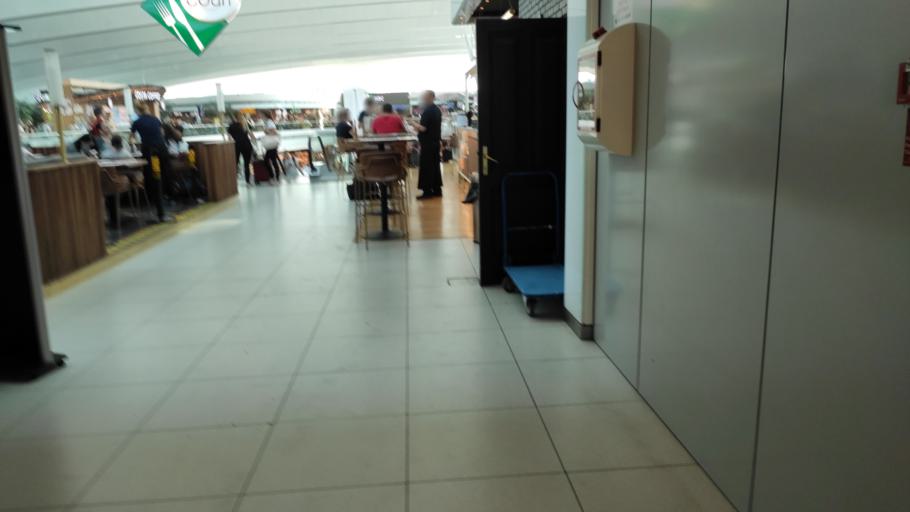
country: HU
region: Pest
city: Vecses
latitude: 47.4335
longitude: 19.2613
